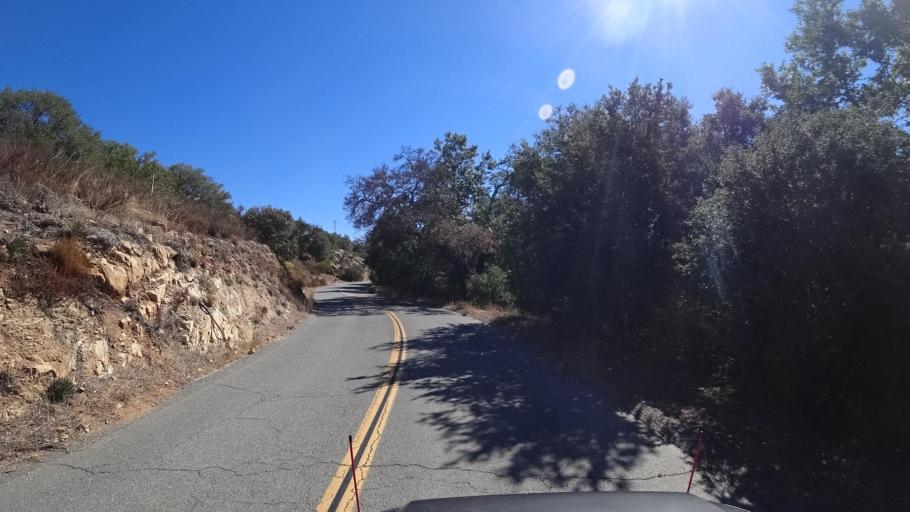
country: US
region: California
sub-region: San Diego County
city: Descanso
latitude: 32.7900
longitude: -116.6628
